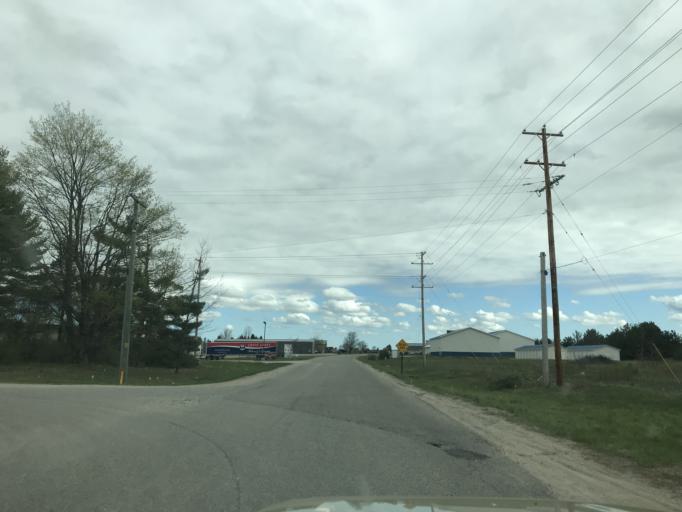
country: US
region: Michigan
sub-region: Otsego County
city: Gaylord
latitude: 45.0339
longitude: -84.6917
